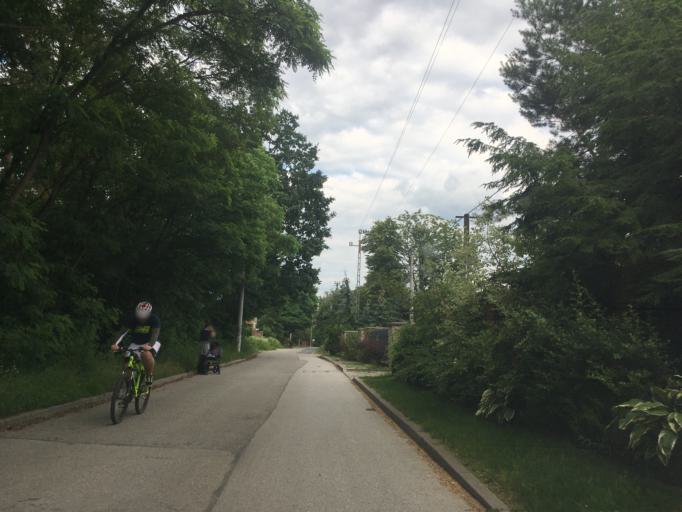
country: PL
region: Masovian Voivodeship
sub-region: Powiat piaseczynski
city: Lesznowola
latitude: 52.0761
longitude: 20.9524
